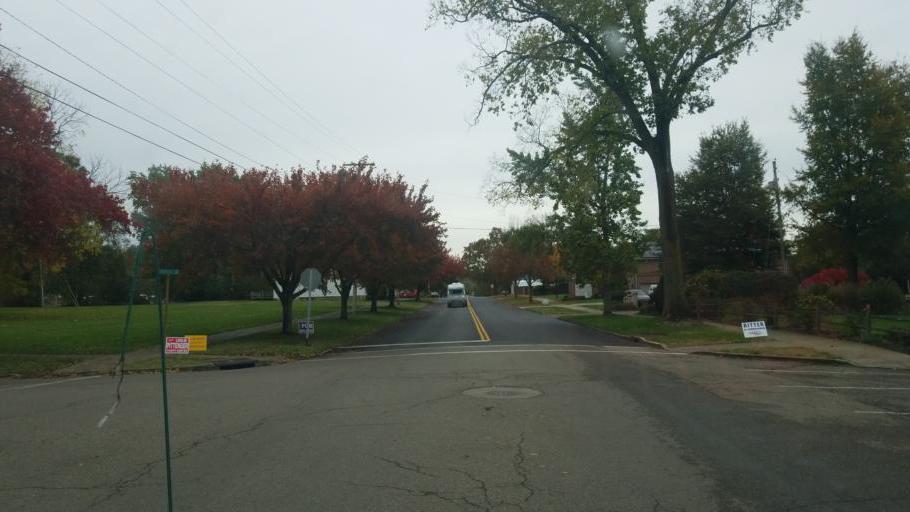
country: US
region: Ohio
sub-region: Washington County
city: Marietta
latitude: 39.4110
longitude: -81.4462
